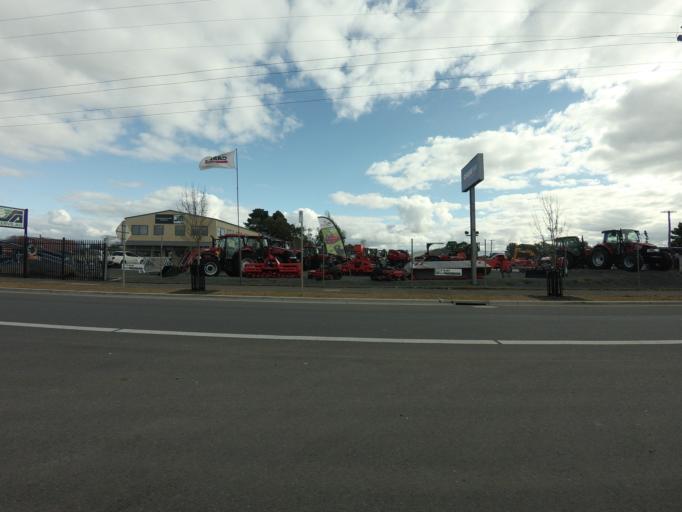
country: AU
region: Tasmania
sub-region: Northern Midlands
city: Longford
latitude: -41.5880
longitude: 147.1194
